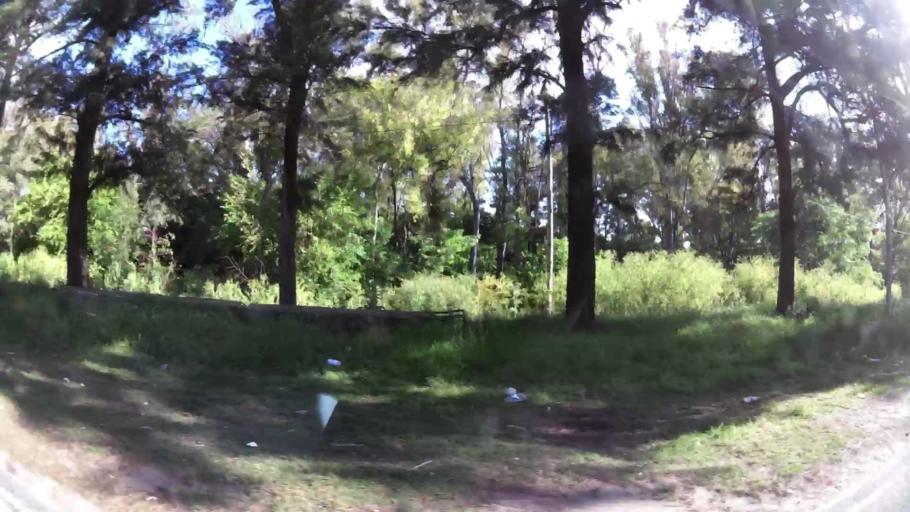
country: AR
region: Buenos Aires
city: Hurlingham
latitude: -34.5629
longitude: -58.6354
